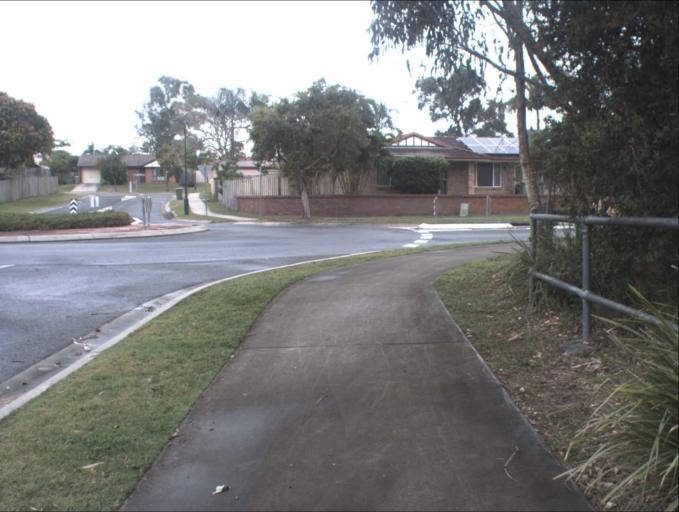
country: AU
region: Queensland
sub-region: Logan
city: Logan City
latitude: -27.6761
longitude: 153.0807
